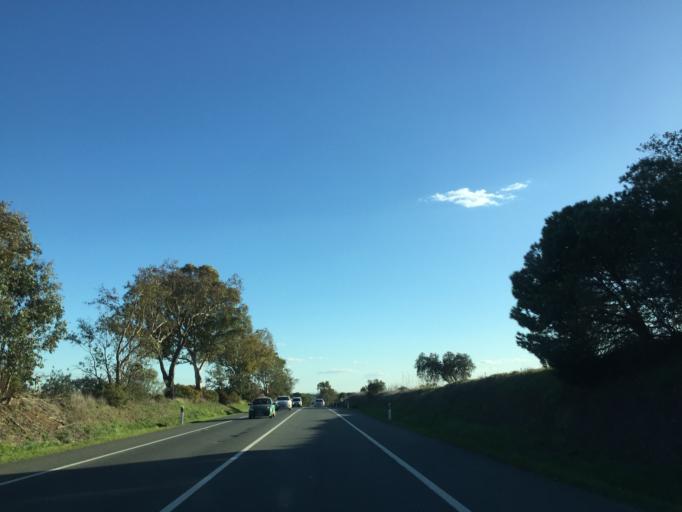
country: PT
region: Setubal
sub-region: Grandola
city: Grandola
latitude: 38.0945
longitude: -8.4185
